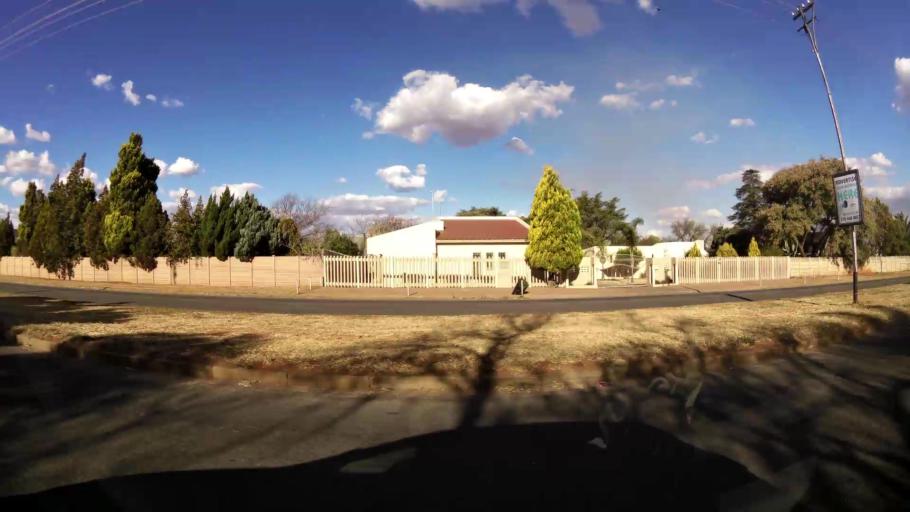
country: ZA
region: North-West
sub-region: Dr Kenneth Kaunda District Municipality
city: Klerksdorp
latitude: -26.8424
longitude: 26.6566
